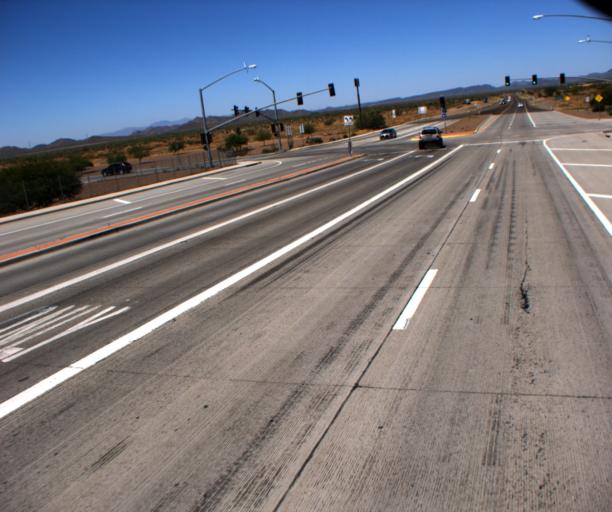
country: US
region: Arizona
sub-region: Maricopa County
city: Anthem
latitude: 33.7983
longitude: -112.1370
